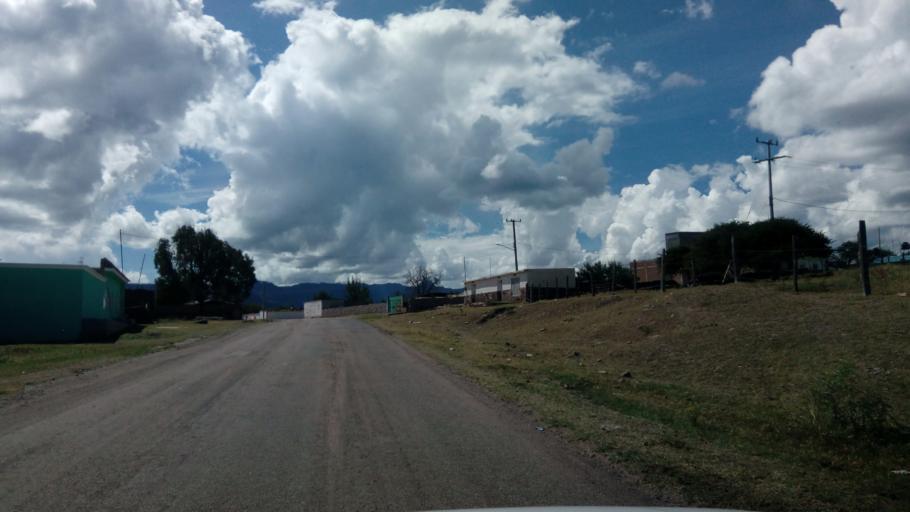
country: MX
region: Durango
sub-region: Durango
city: Jose Refugio Salcido
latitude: 23.7943
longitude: -104.4864
